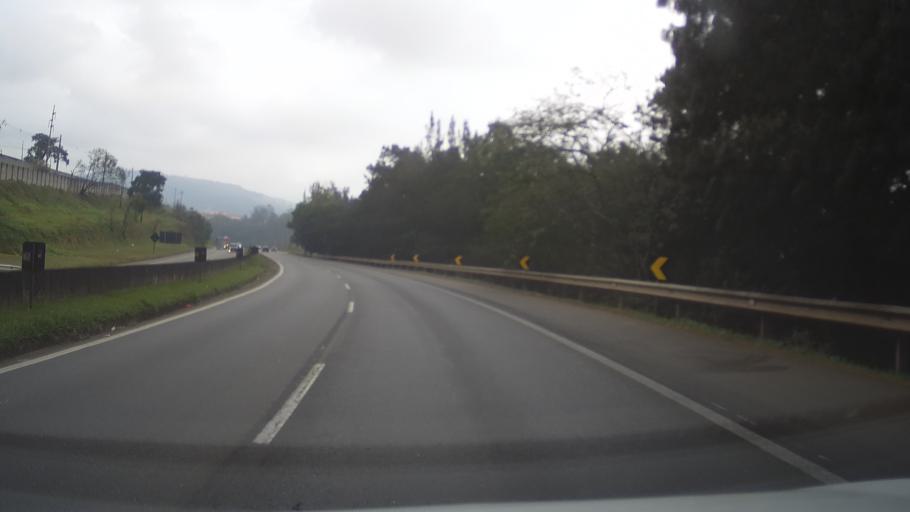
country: BR
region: Minas Gerais
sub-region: Extrema
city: Extrema
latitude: -22.8566
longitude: -46.3369
